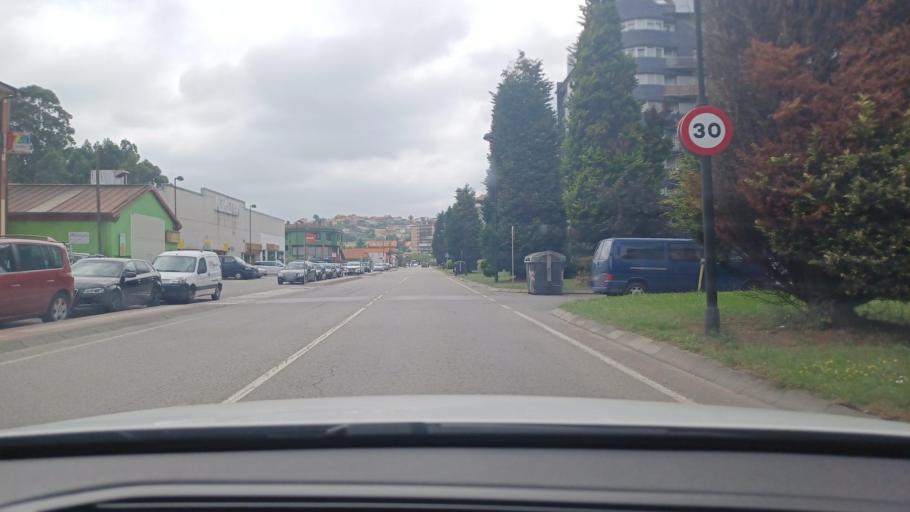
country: ES
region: Asturias
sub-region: Province of Asturias
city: Aviles
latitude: 43.5722
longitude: -5.9547
